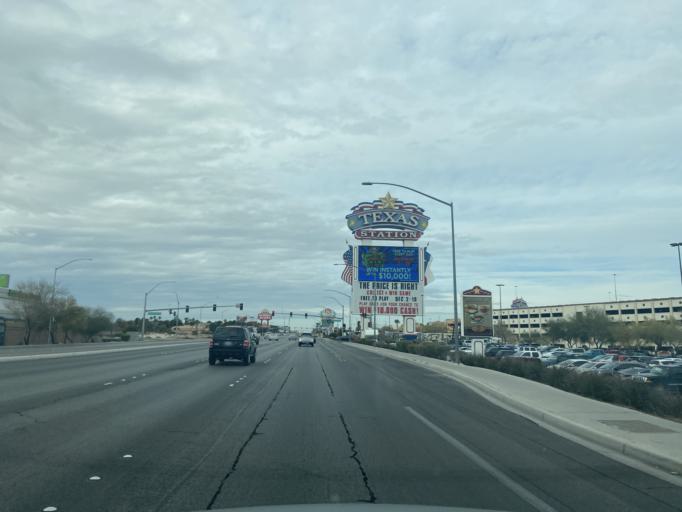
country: US
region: Nevada
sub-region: Clark County
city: Las Vegas
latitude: 36.1971
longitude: -115.1937
